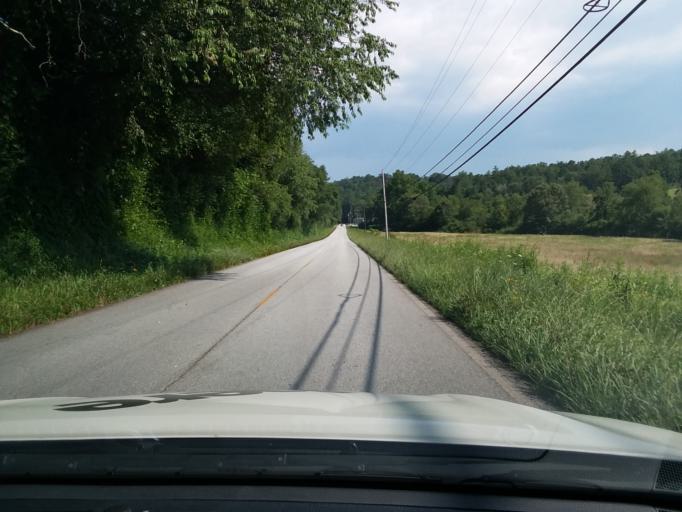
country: US
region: Georgia
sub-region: Rabun County
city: Clayton
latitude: 34.8357
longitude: -83.4334
